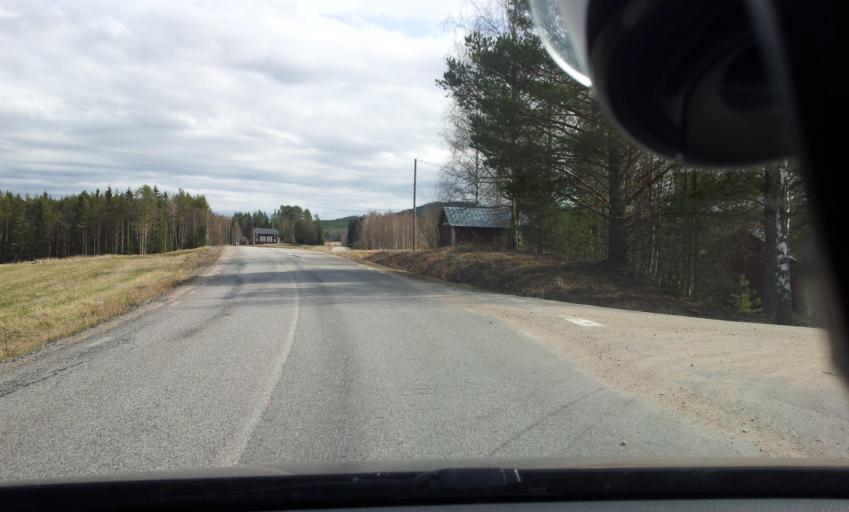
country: SE
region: Gaevleborg
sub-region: Ljusdals Kommun
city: Farila
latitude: 61.7705
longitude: 15.9670
